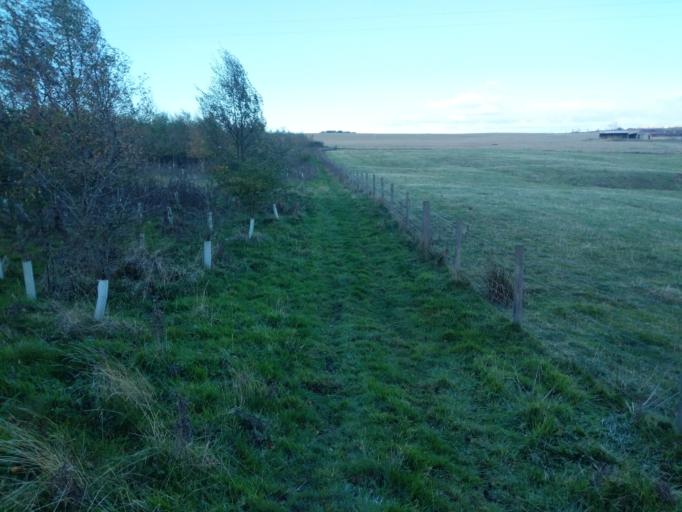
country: GB
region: England
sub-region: County Durham
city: Tow Law
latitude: 54.7308
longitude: -1.7700
